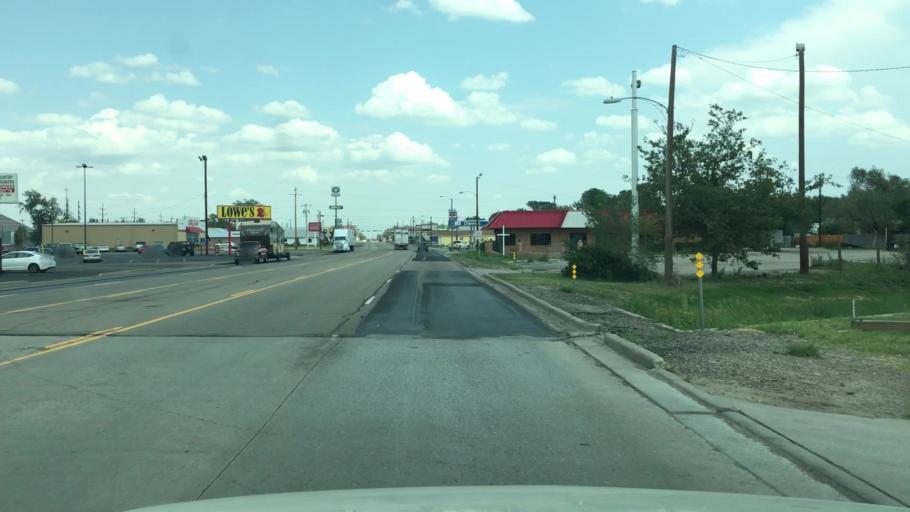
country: US
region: Texas
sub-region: Donley County
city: Clarendon
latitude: 34.9406
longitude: -100.8937
